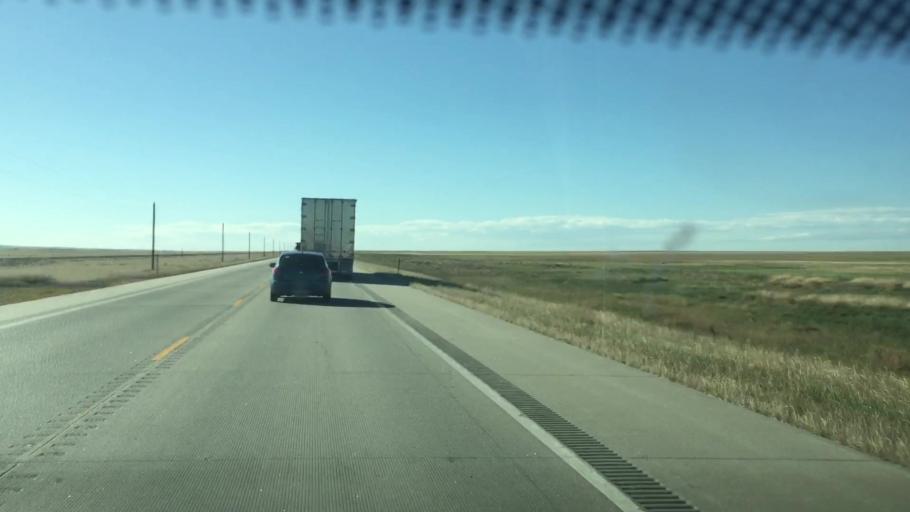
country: US
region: Colorado
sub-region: Kiowa County
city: Eads
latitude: 38.8308
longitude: -103.0424
